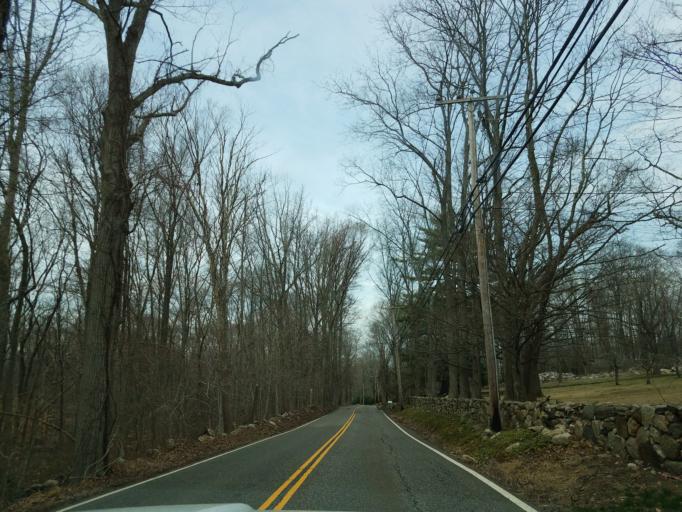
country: US
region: Connecticut
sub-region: Fairfield County
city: Glenville
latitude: 41.1005
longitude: -73.6504
